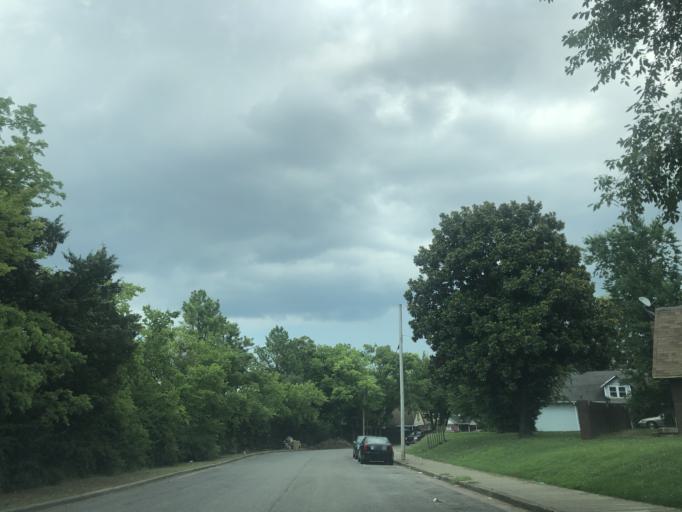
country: US
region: Tennessee
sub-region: Davidson County
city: Nashville
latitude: 36.1667
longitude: -86.8162
